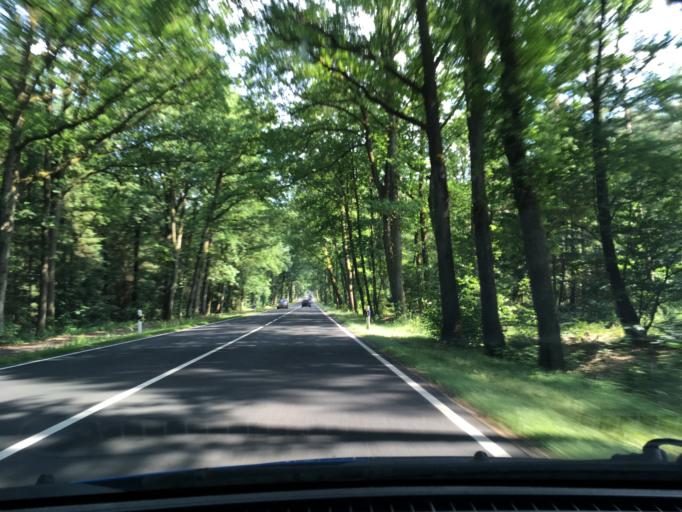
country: DE
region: Lower Saxony
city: Welle
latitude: 53.2226
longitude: 9.8094
